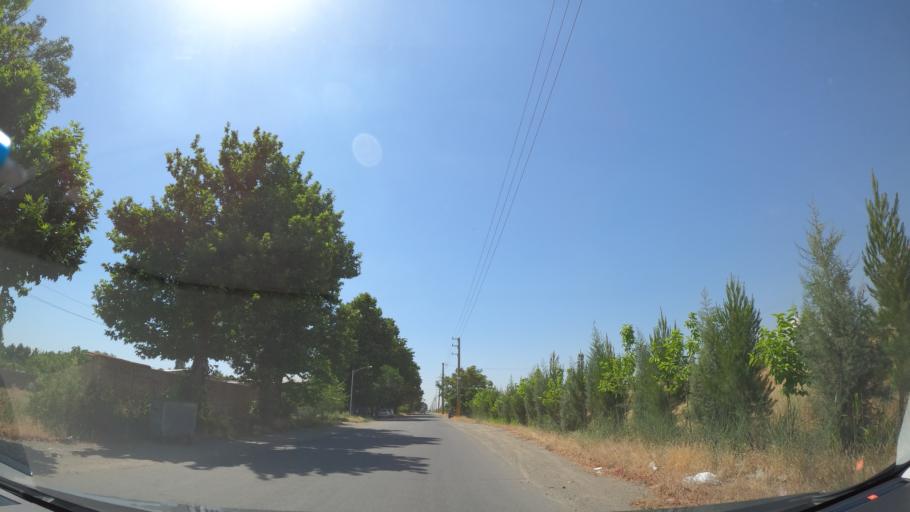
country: IR
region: Alborz
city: Hashtgerd
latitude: 35.9163
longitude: 50.7316
